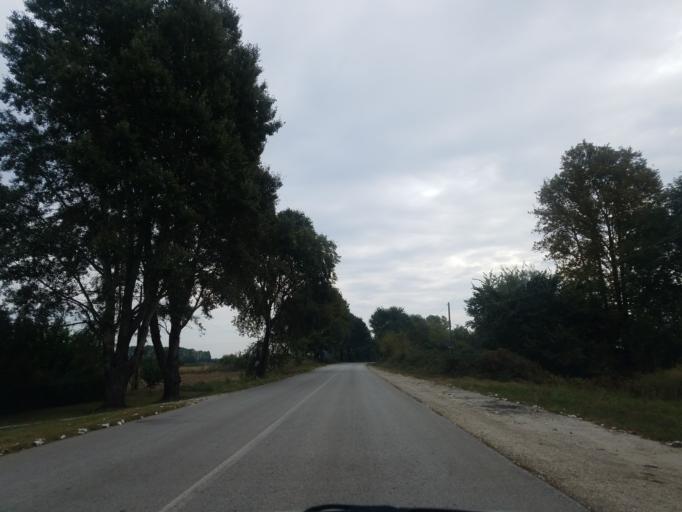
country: GR
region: Thessaly
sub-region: Nomos Kardhitsas
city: Agnantero
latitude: 39.4584
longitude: 21.8611
